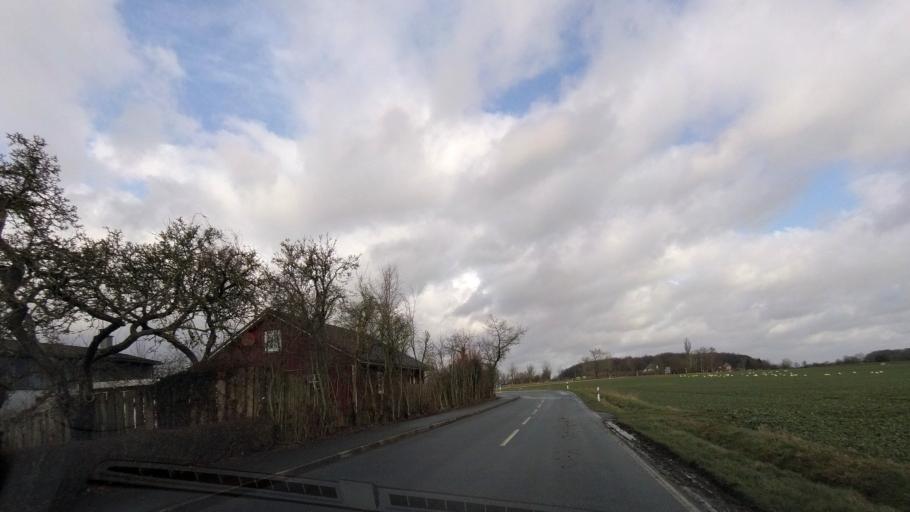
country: DE
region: Schleswig-Holstein
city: Rabenkirchen-Fauluck
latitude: 54.6427
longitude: 9.8741
